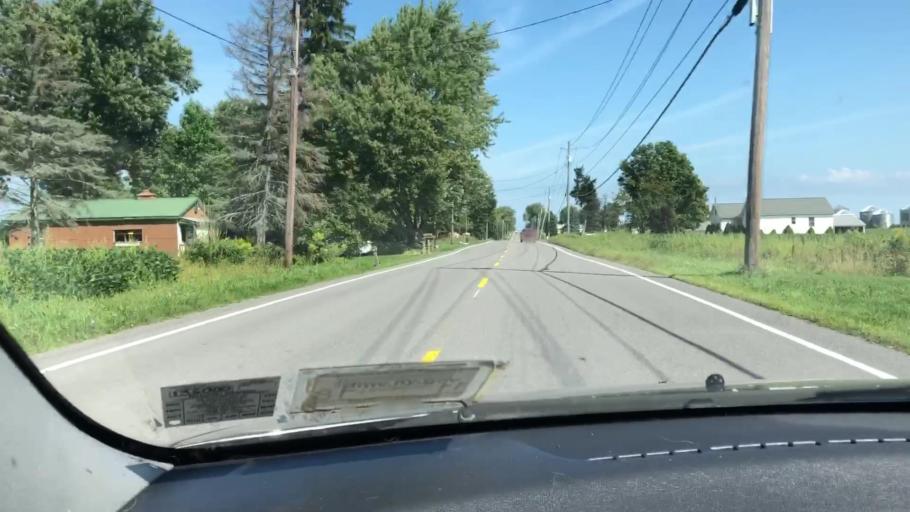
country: US
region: New York
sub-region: Wayne County
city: Macedon
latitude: 43.1015
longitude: -77.3207
